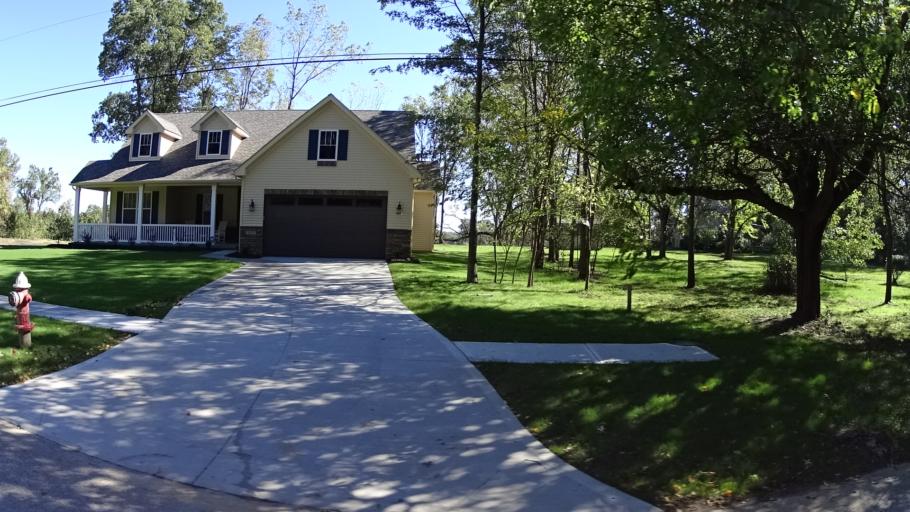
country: US
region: Ohio
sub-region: Lorain County
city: Amherst
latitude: 41.4054
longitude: -82.2529
